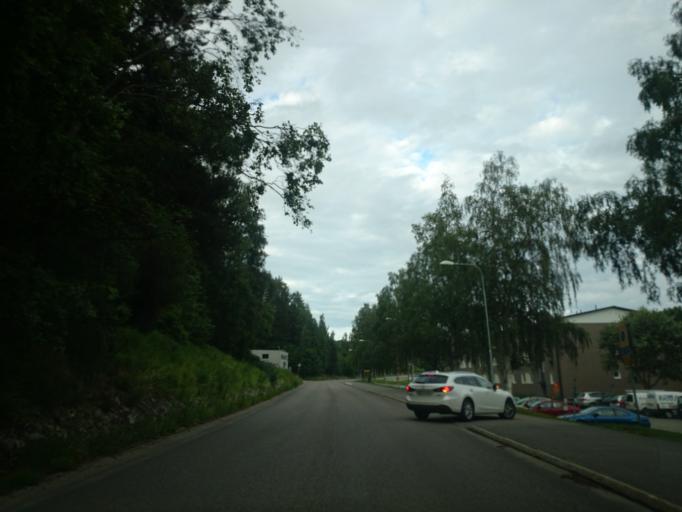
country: SE
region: Vaesternorrland
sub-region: Sundsvalls Kommun
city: Sundsvall
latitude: 62.4068
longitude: 17.2491
